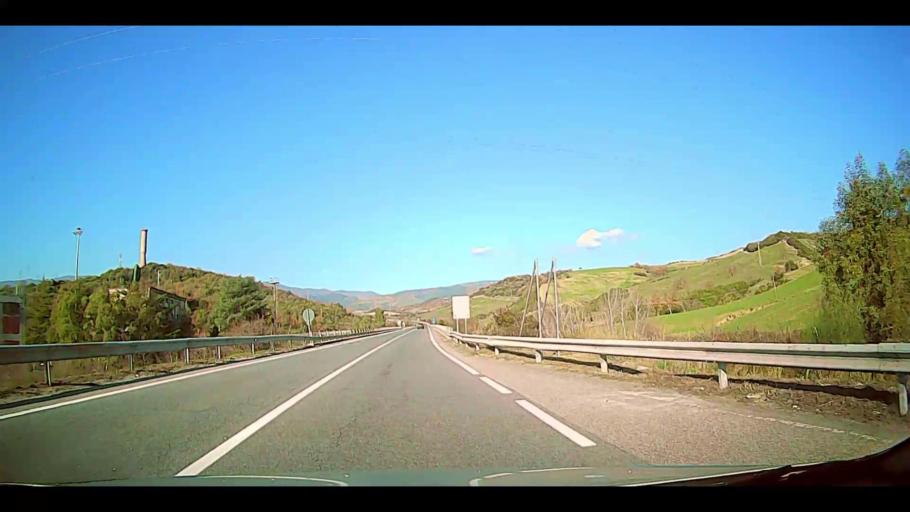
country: IT
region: Calabria
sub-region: Provincia di Crotone
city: Roccabernarda
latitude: 39.1855
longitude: 16.8350
